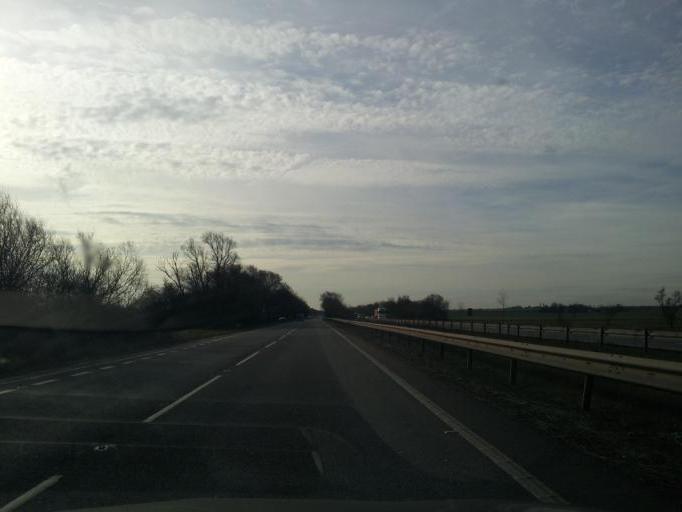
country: GB
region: England
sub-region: Cambridgeshire
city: Brampton
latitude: 52.3256
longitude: -0.2465
